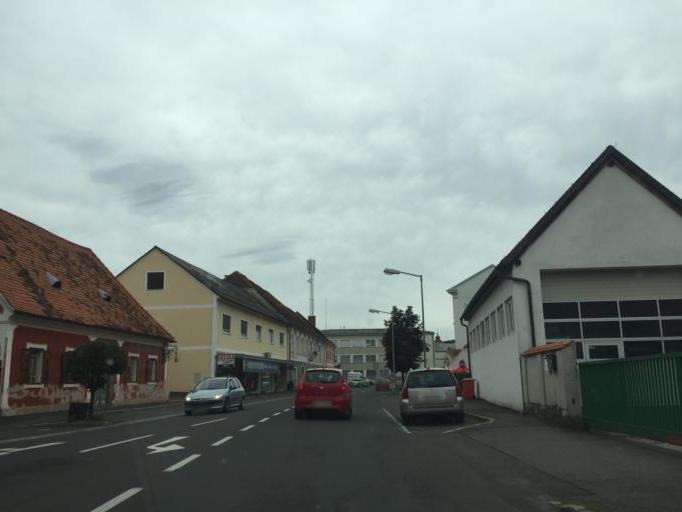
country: AT
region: Styria
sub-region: Politischer Bezirk Suedoststeiermark
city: Mureck
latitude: 46.7077
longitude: 15.7695
